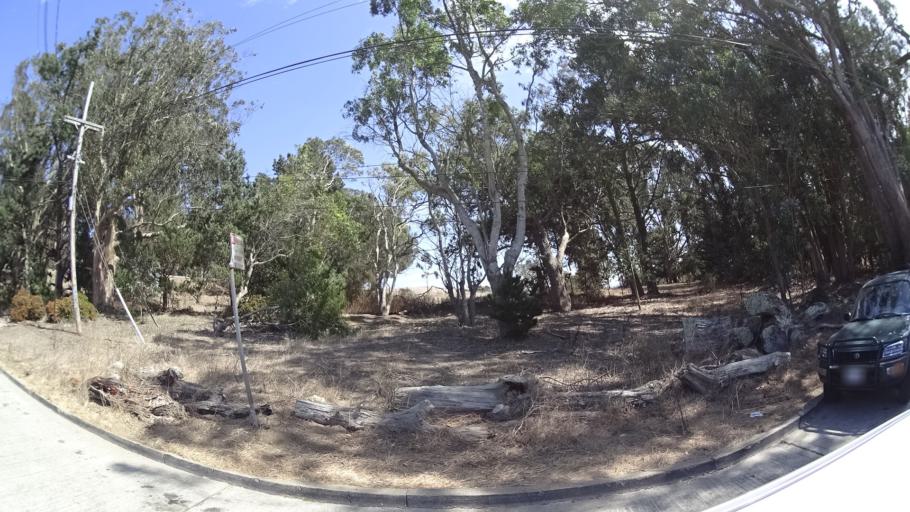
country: US
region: California
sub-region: San Mateo County
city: Daly City
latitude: 37.7157
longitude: -122.4272
